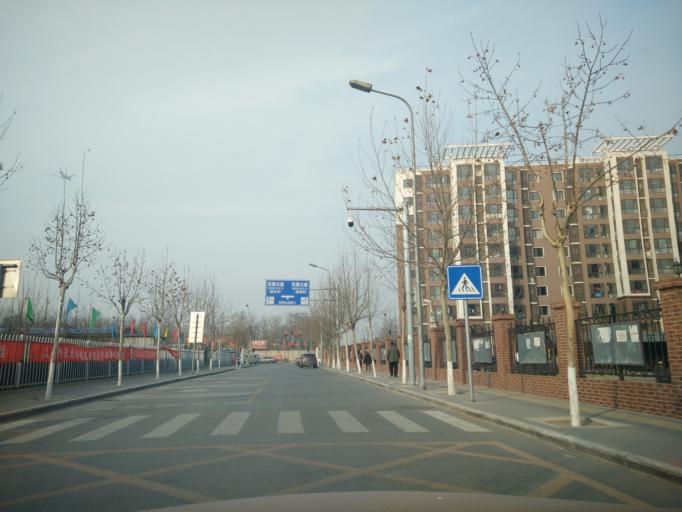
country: CN
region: Beijing
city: Yinghai
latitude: 39.7159
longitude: 116.3964
